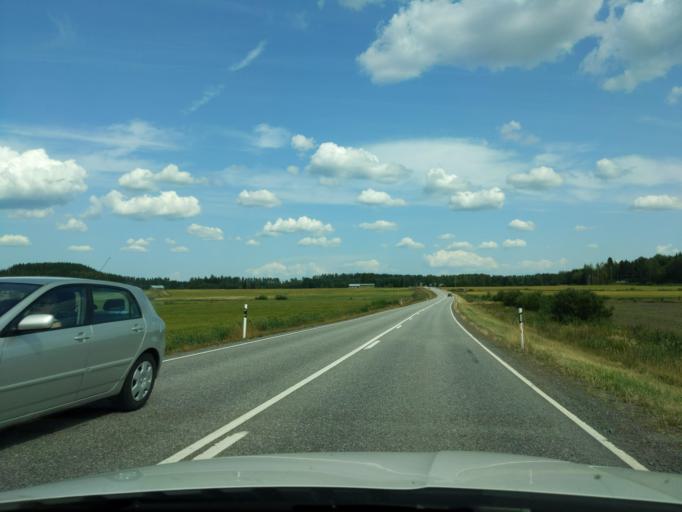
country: FI
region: Haeme
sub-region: Haemeenlinna
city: Lammi
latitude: 61.1228
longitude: 24.9462
